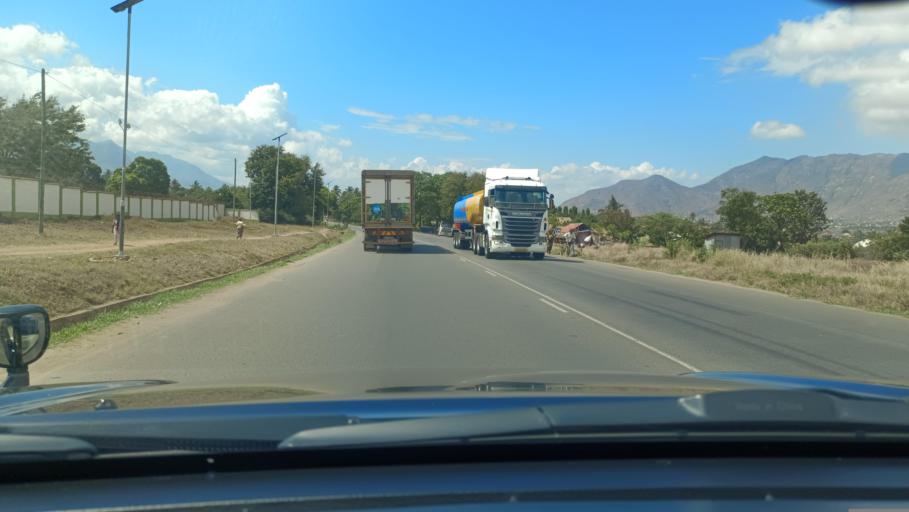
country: TZ
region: Morogoro
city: Morogoro
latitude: -6.8115
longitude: 37.6511
